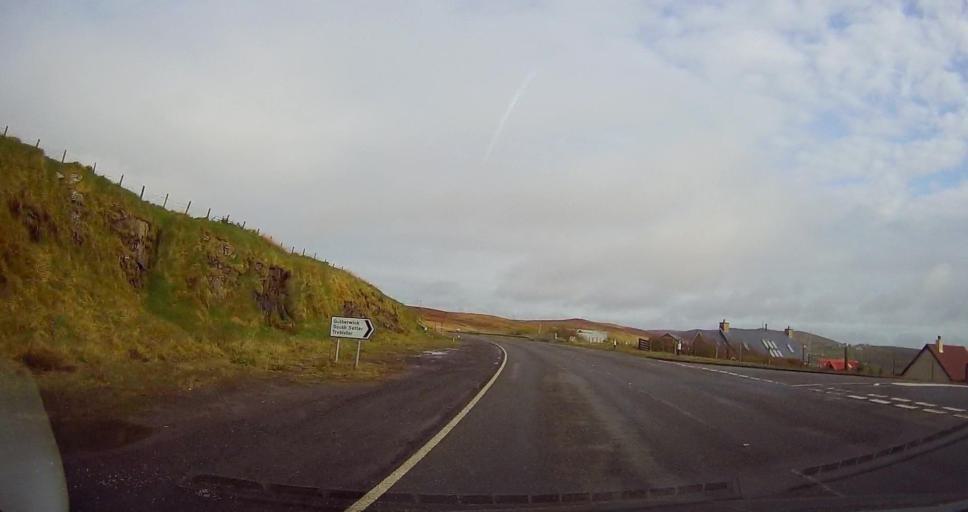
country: GB
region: Scotland
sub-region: Shetland Islands
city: Lerwick
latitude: 60.1207
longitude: -1.2150
